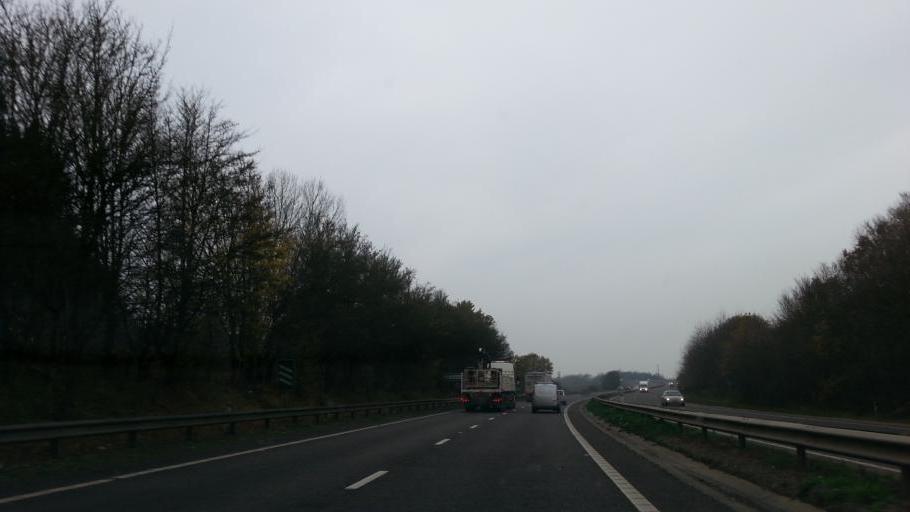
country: GB
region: England
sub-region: Suffolk
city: Bury St Edmunds
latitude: 52.2534
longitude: 0.6842
